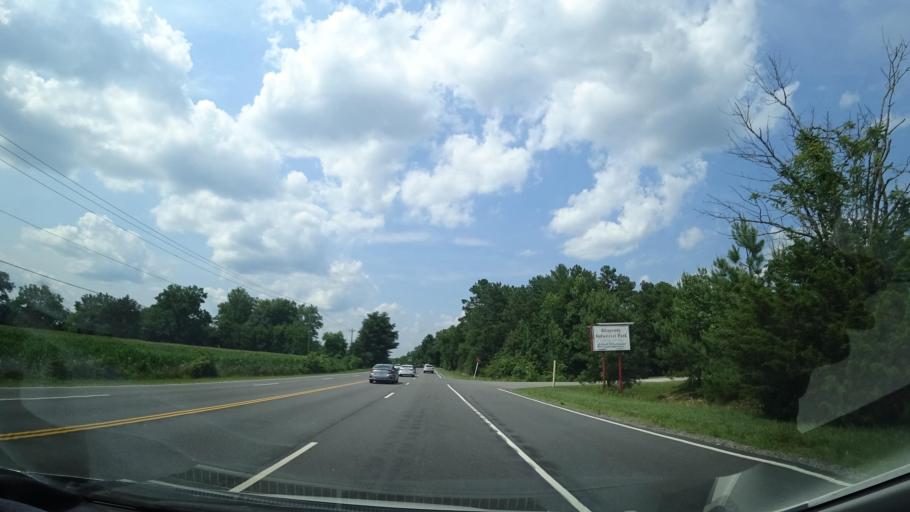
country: US
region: Virginia
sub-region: Hanover County
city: Ashland
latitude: 37.8813
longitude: -77.4645
